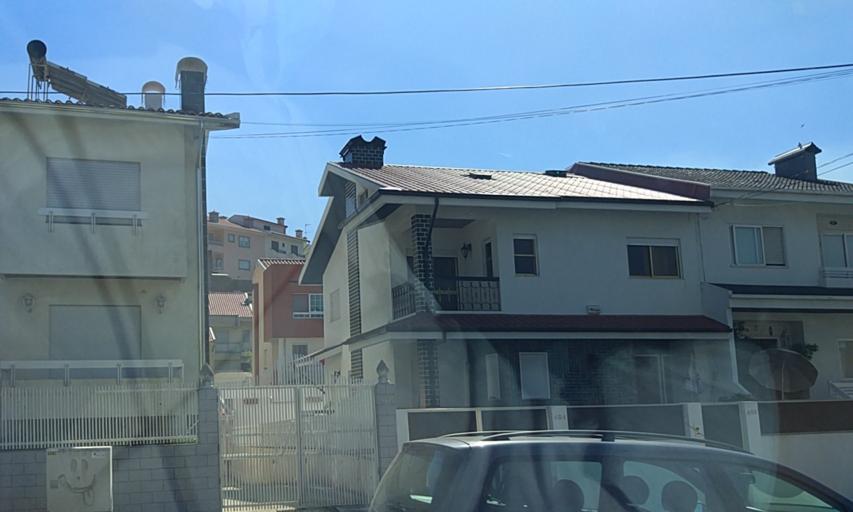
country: PT
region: Porto
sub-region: Valongo
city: Valongo
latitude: 41.1885
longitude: -8.5252
